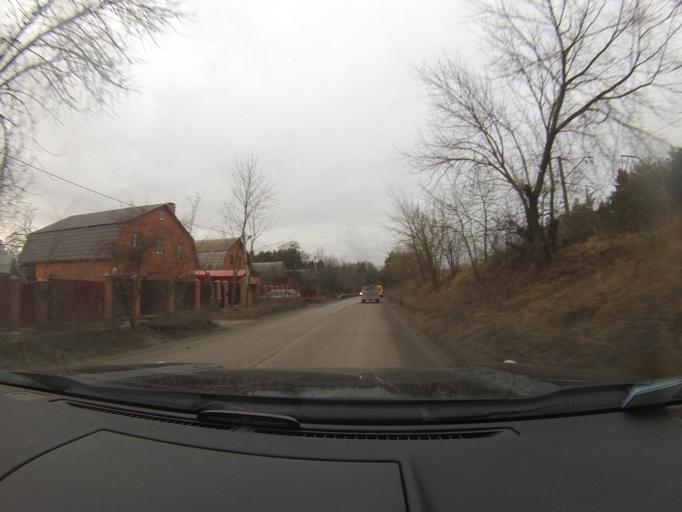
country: RU
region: Moskovskaya
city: Voskresensk
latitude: 55.3312
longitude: 38.6785
